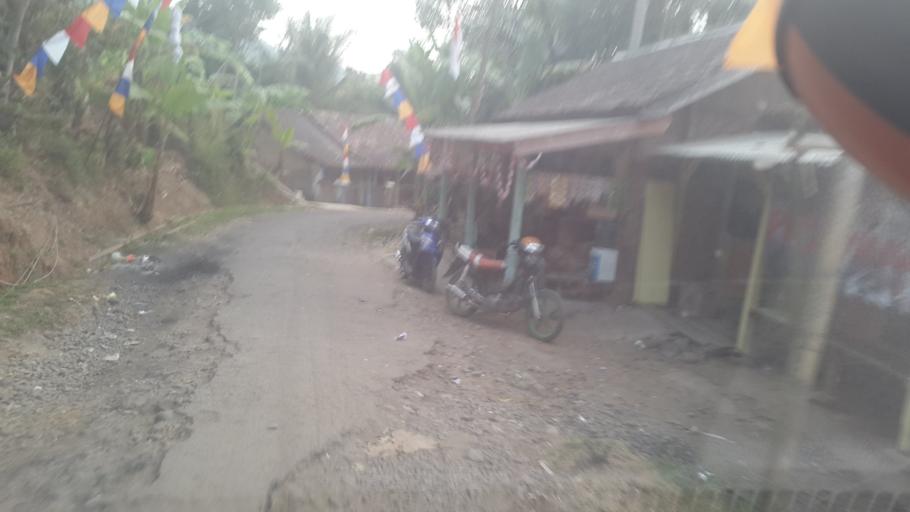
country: ID
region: West Java
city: Sukamaju
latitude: -7.0057
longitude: 106.9024
